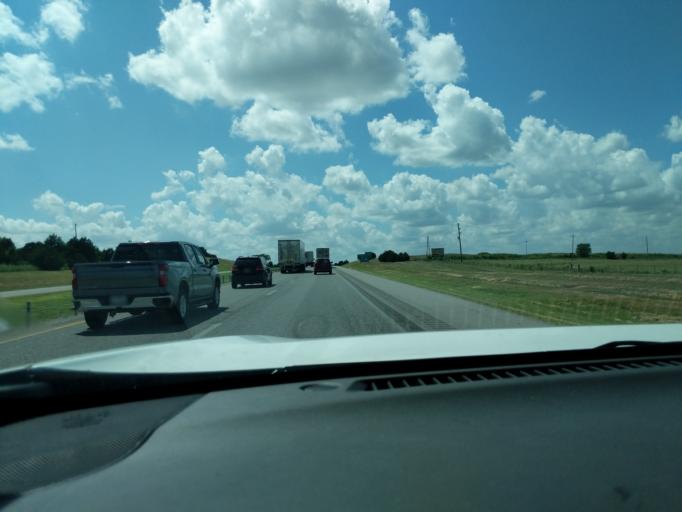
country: US
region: Oklahoma
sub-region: Caddo County
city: Hinton
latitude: 35.5268
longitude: -98.3218
